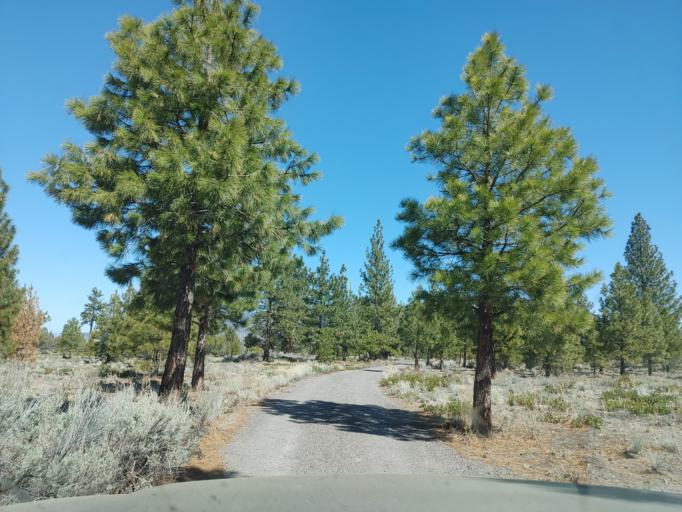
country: US
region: California
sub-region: Siskiyou County
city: Weed
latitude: 41.5452
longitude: -122.2324
